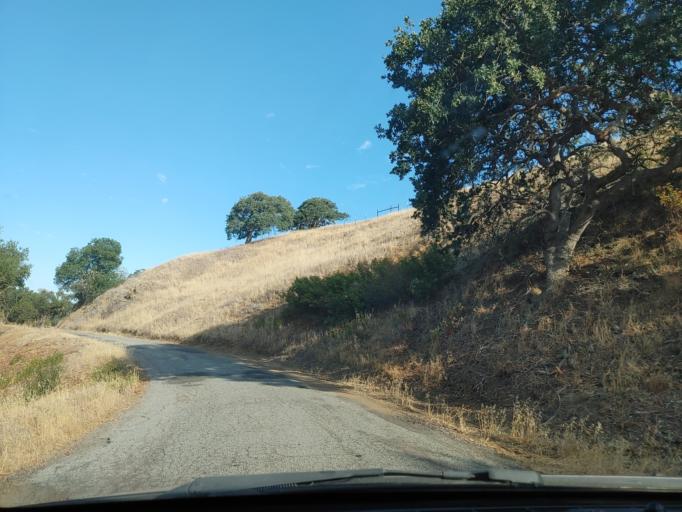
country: US
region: California
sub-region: San Benito County
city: Ridgemark
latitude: 36.7722
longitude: -121.2235
